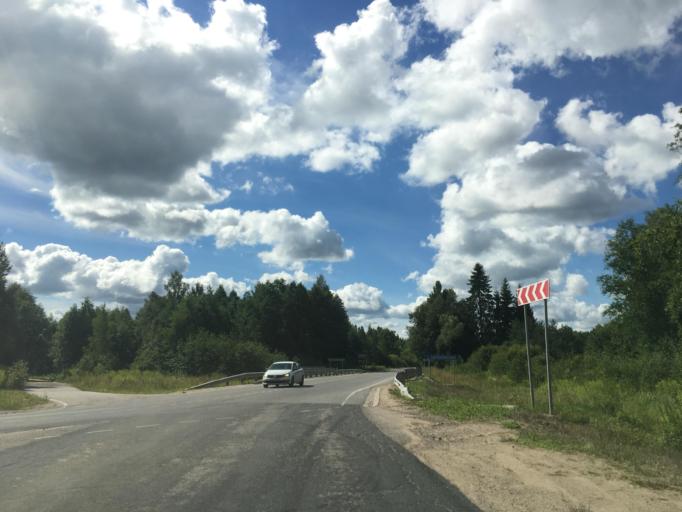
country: RU
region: Pskov
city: Pskov
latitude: 57.6958
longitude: 28.1800
